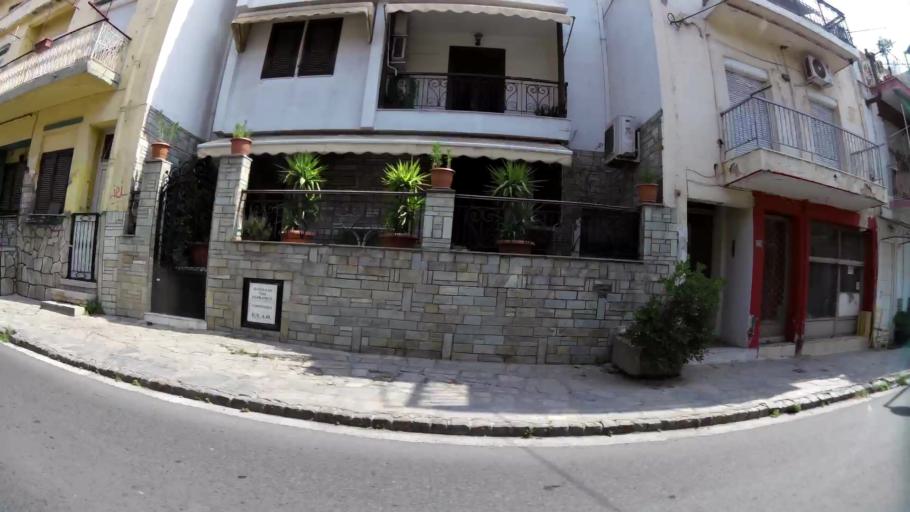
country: GR
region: Central Macedonia
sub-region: Nomos Thessalonikis
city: Agios Pavlos
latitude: 40.6408
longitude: 22.9575
